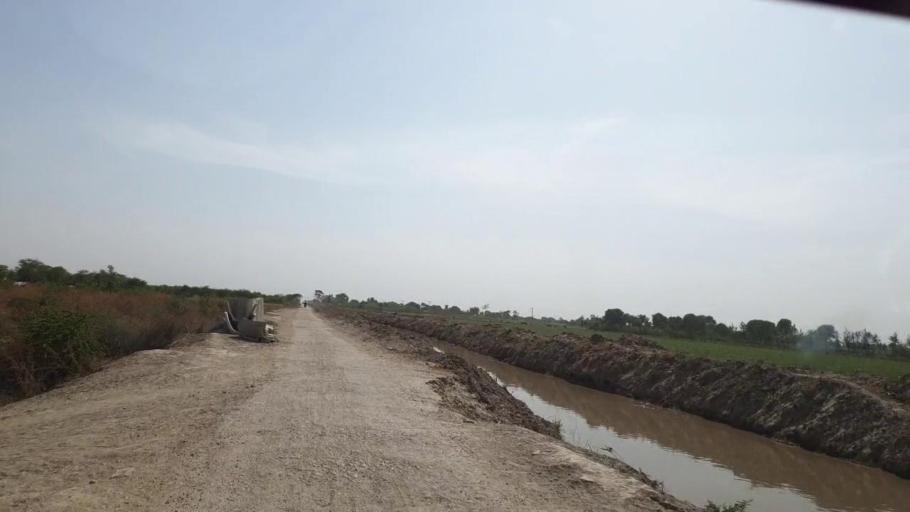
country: PK
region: Sindh
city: Nabisar
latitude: 25.0814
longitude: 69.5800
